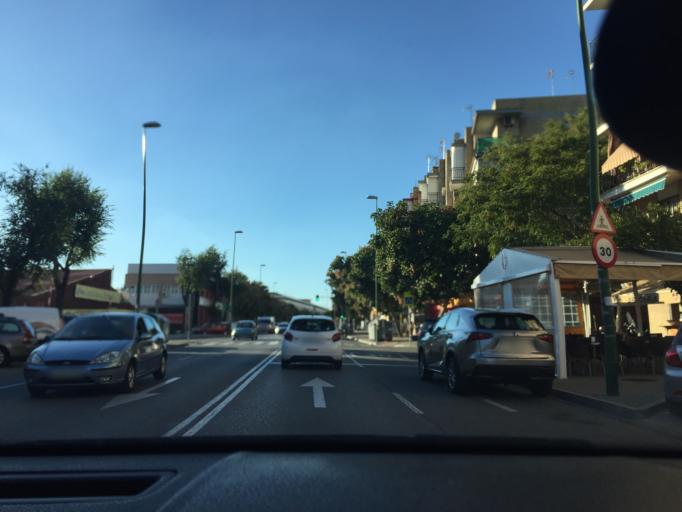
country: ES
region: Andalusia
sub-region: Provincia de Sevilla
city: Sevilla
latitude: 37.3680
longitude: -5.9552
